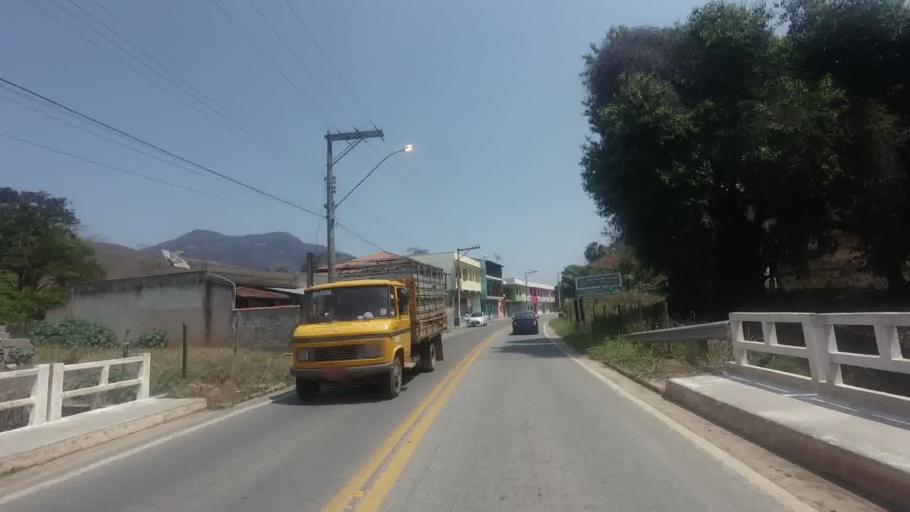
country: BR
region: Espirito Santo
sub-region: Mimoso Do Sul
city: Mimoso do Sul
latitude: -20.9431
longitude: -41.3337
